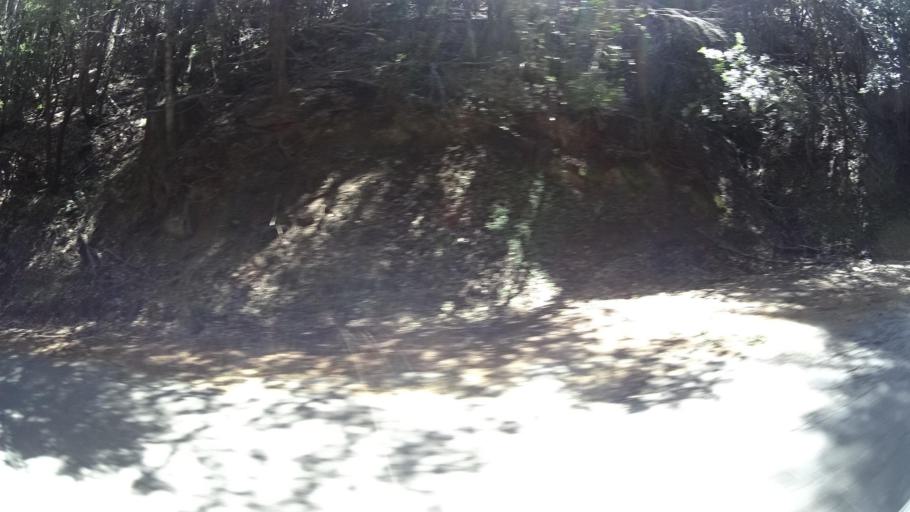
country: US
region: California
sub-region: Humboldt County
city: Rio Dell
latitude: 40.2845
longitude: -124.0611
